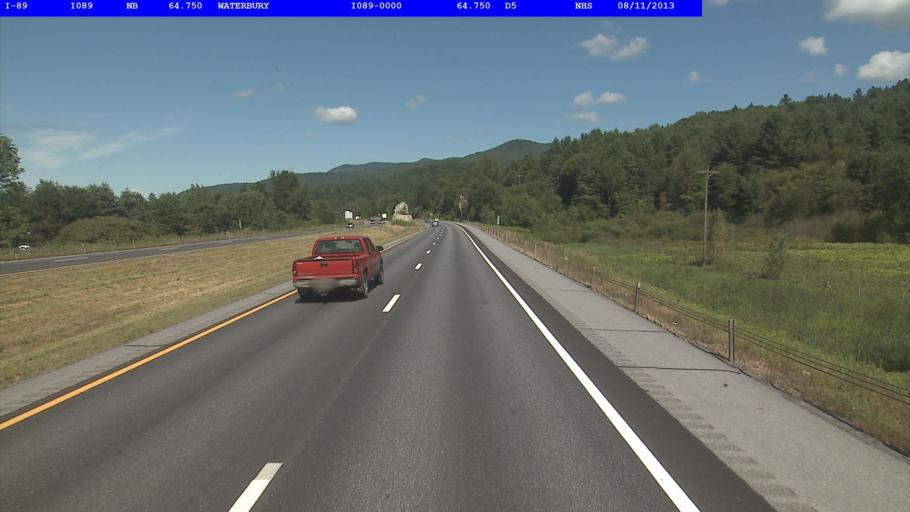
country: US
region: Vermont
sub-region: Washington County
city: Waterbury
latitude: 44.3486
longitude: -72.7698
